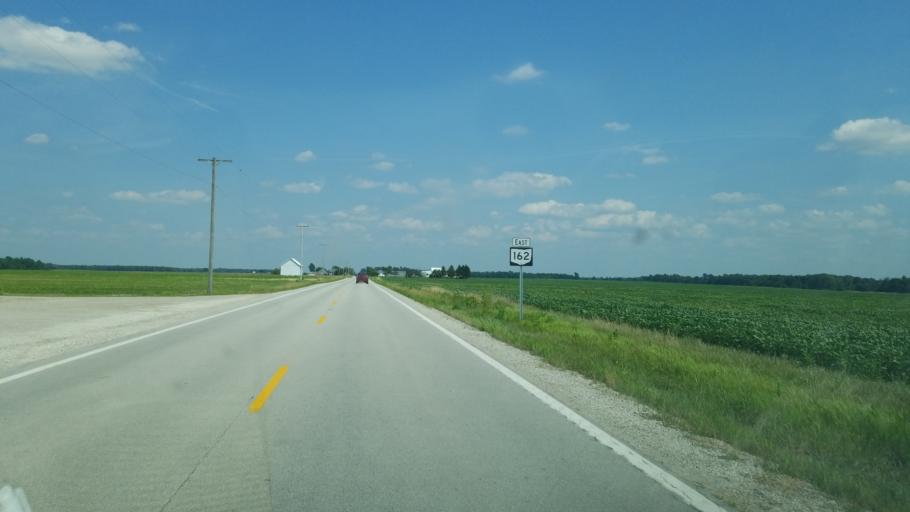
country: US
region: Ohio
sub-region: Sandusky County
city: Mount Carmel
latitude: 41.1246
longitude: -82.8999
